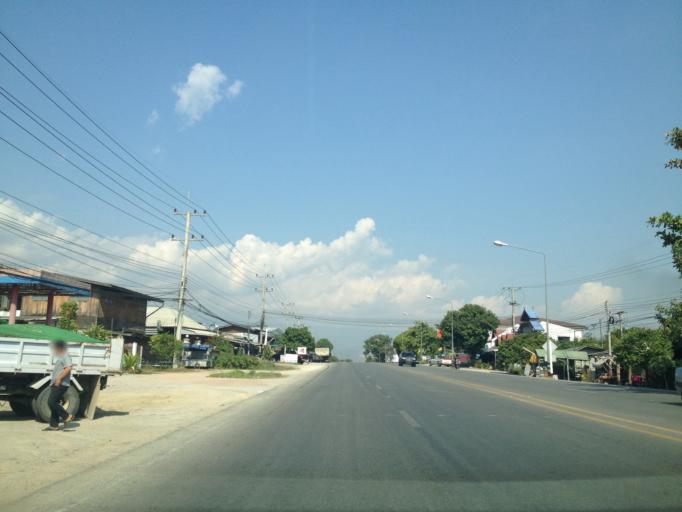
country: TH
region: Chiang Mai
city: Hot
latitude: 18.2078
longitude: 98.6165
